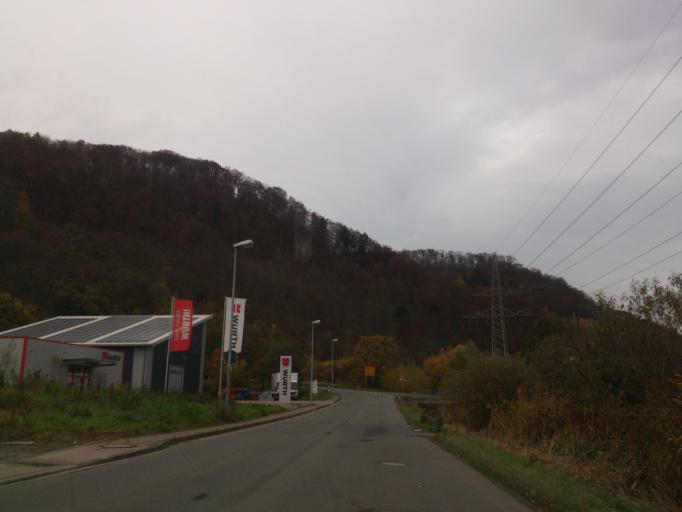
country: DE
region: North Rhine-Westphalia
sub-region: Regierungsbezirk Detmold
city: Hoexter
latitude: 51.7891
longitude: 9.3947
